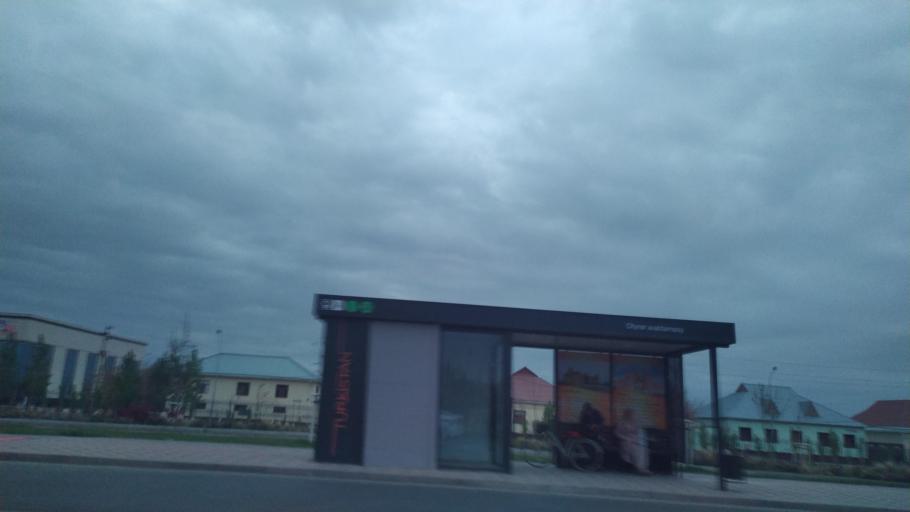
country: KZ
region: Ongtustik Qazaqstan
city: Turkestan
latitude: 43.2824
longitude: 68.3151
